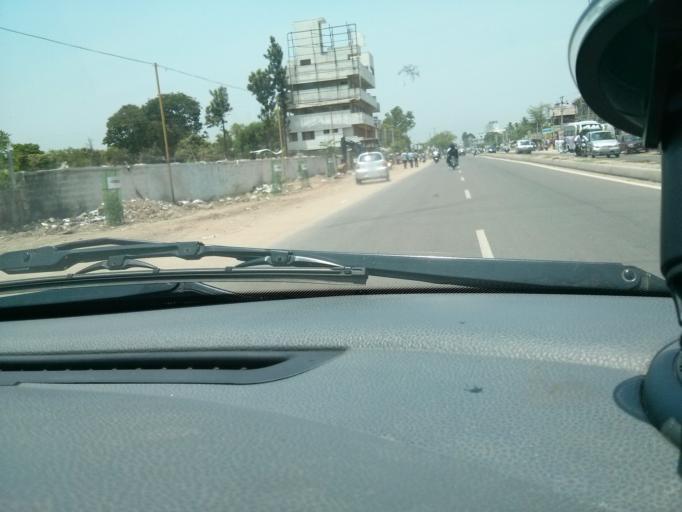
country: IN
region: Tamil Nadu
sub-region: Coimbatore
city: Coimbatore
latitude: 11.0755
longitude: 76.9419
